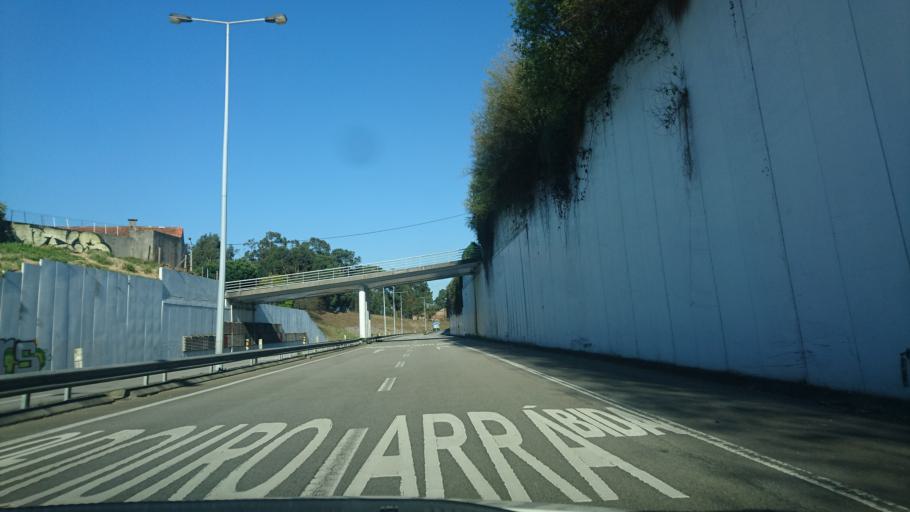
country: PT
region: Porto
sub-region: Vila Nova de Gaia
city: Oliveira do Douro
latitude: 41.1293
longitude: -8.5944
